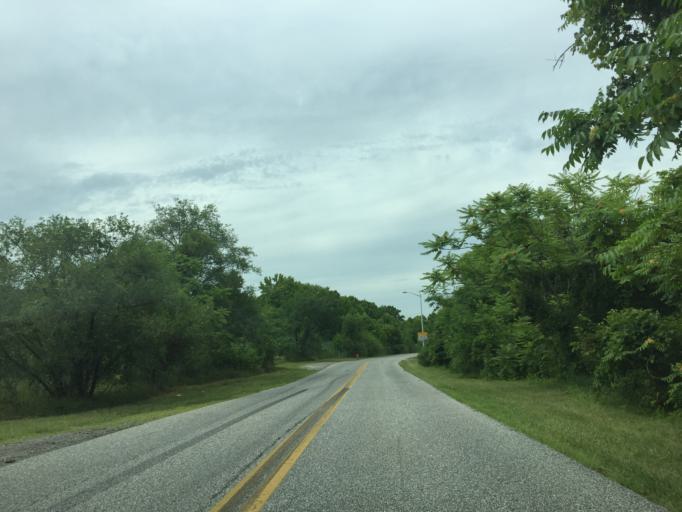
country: US
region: Maryland
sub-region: Baltimore County
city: Edgemere
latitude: 39.2608
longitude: -76.4557
